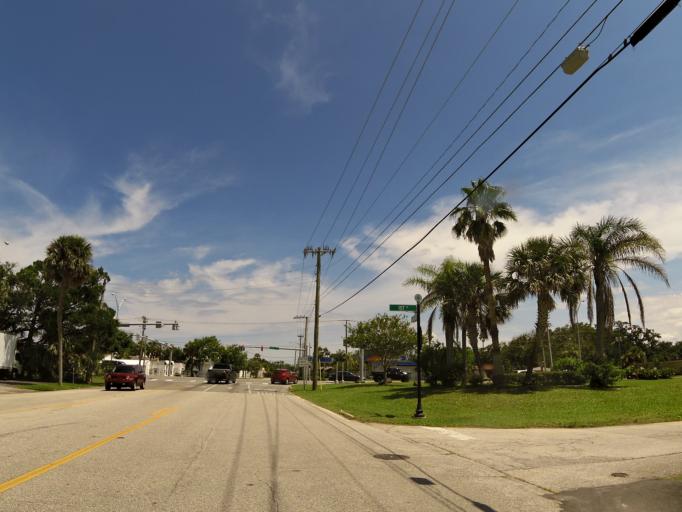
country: US
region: Florida
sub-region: Volusia County
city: Holly Hill
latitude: 29.2290
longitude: -81.0273
